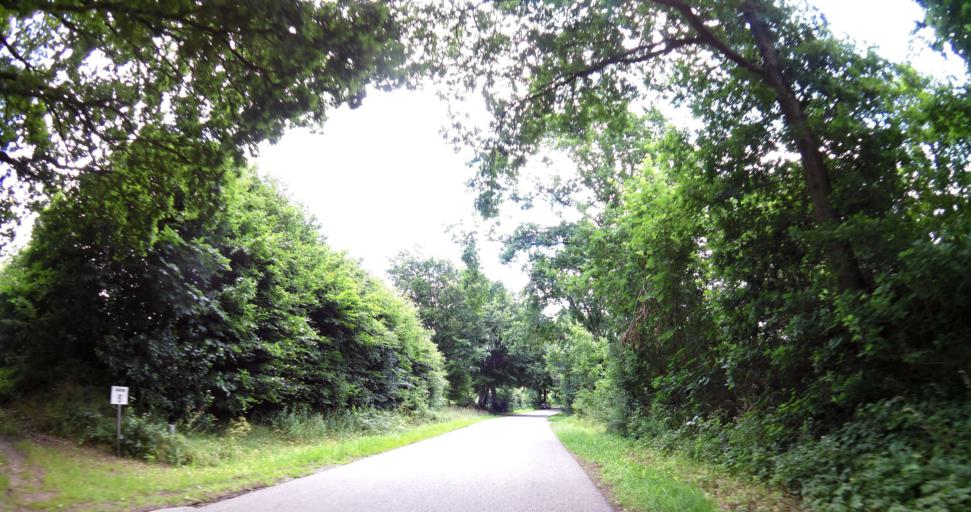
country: DE
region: Schleswig-Holstein
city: Fleckeby
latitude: 54.4986
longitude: 9.7290
